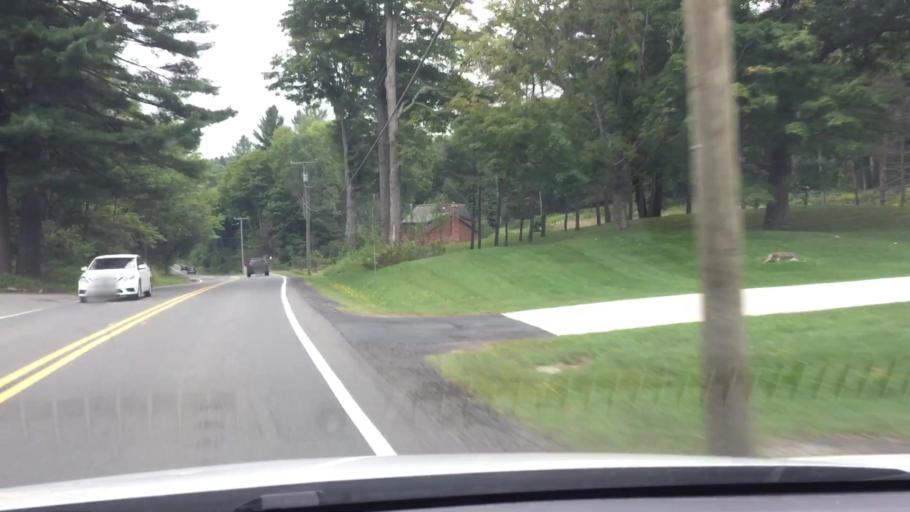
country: US
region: Massachusetts
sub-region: Berkshire County
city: Hinsdale
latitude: 42.3846
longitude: -73.1225
